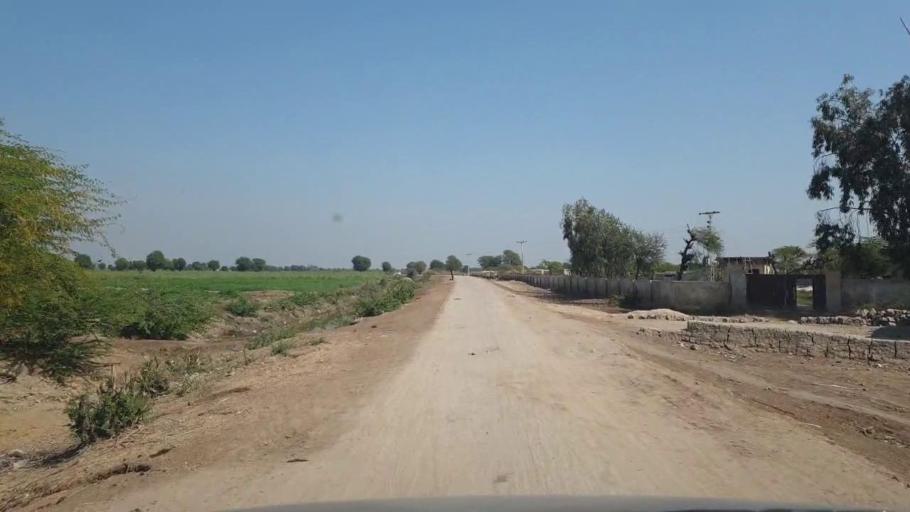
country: PK
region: Sindh
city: Digri
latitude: 25.0911
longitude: 69.2332
